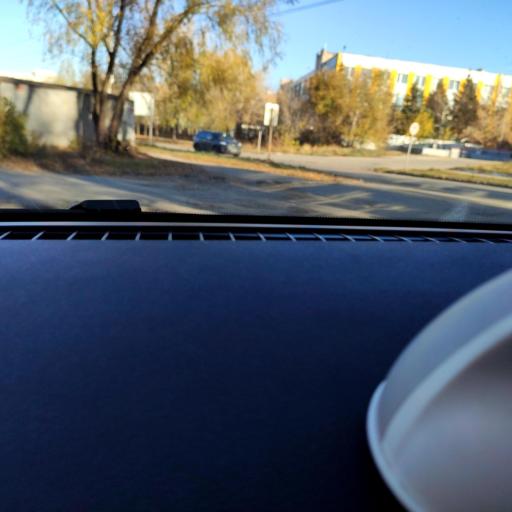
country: RU
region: Samara
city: Samara
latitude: 53.1871
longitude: 50.1734
